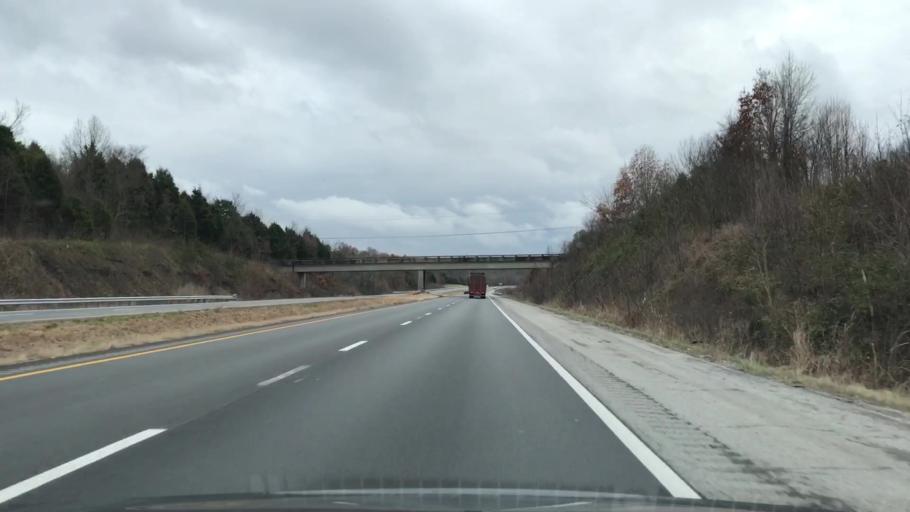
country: US
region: Kentucky
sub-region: Hopkins County
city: Madisonville
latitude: 37.3968
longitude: -87.4761
